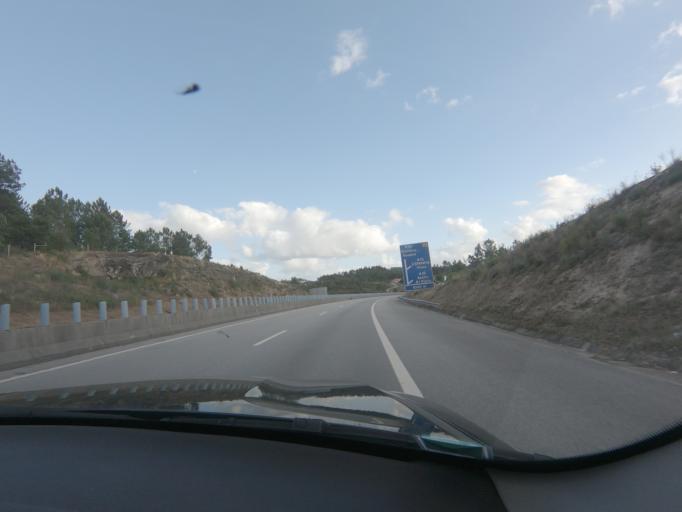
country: PT
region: Viseu
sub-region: Viseu
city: Viseu
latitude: 40.6376
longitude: -7.9579
